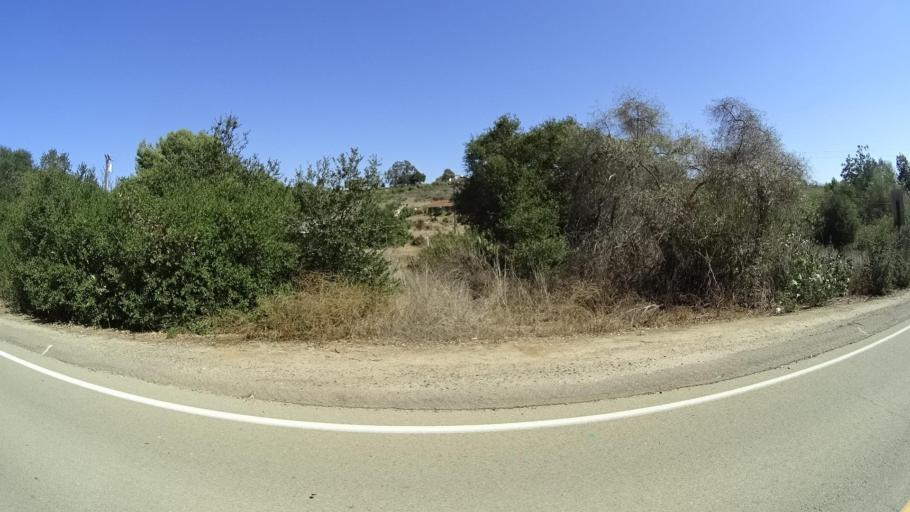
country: US
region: California
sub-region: San Diego County
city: Bonsall
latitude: 33.2957
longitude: -117.1777
